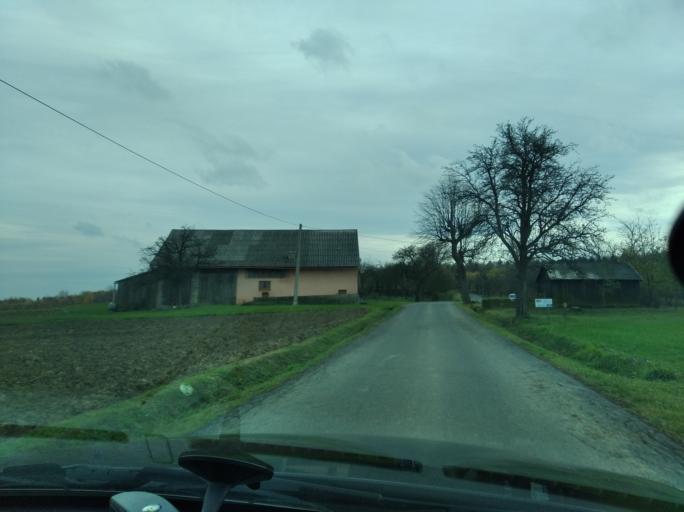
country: PL
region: Subcarpathian Voivodeship
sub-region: Powiat strzyzowski
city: Strzyzow
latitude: 49.9127
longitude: 21.7717
